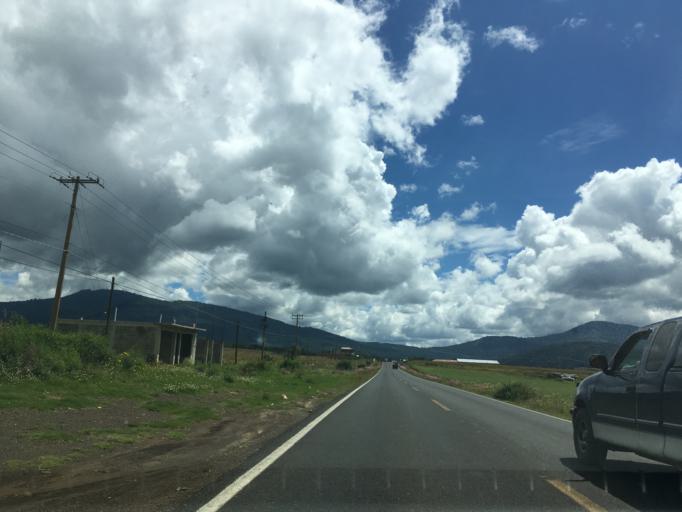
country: MX
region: Michoacan
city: Cheran
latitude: 19.6689
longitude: -101.9456
